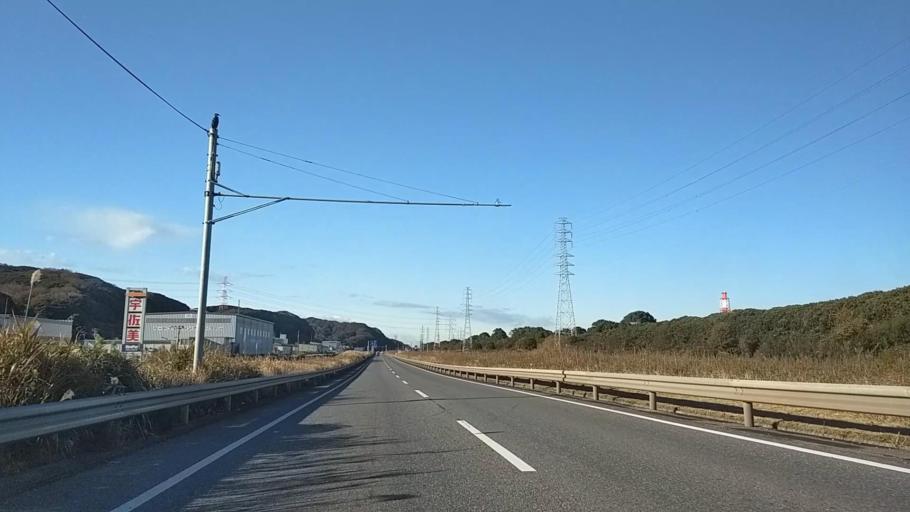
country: JP
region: Chiba
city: Kimitsu
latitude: 35.3503
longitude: 139.8968
